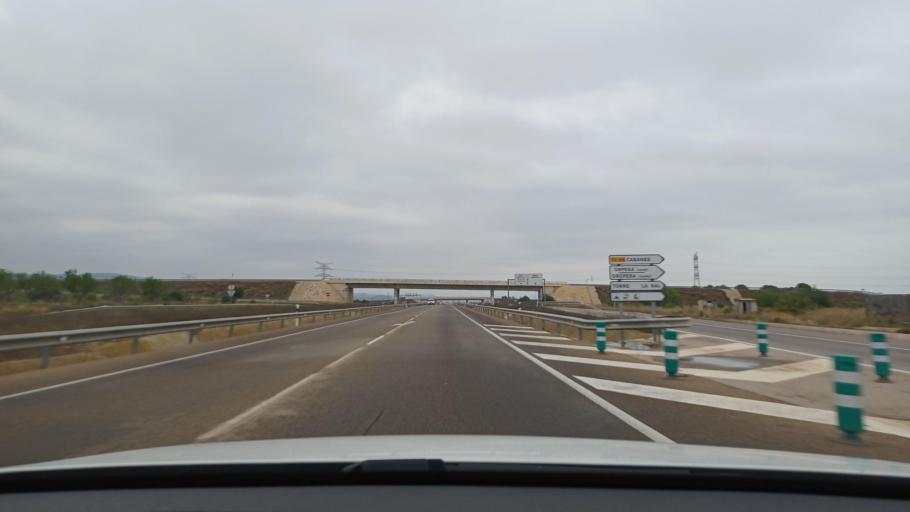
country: ES
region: Valencia
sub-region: Provincia de Castello
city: Orpesa/Oropesa del Mar
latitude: 40.1204
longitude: 0.1427
